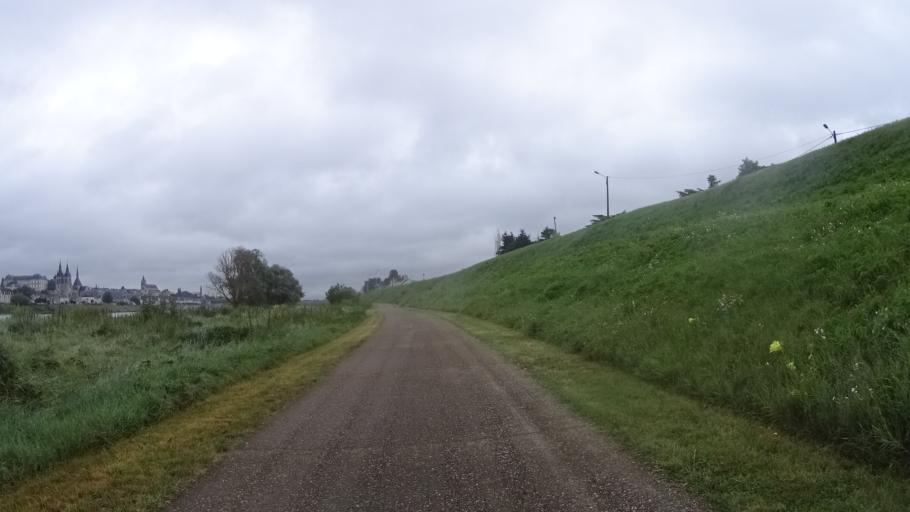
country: FR
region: Centre
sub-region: Departement du Loir-et-Cher
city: Blois
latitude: 47.5767
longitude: 1.3276
